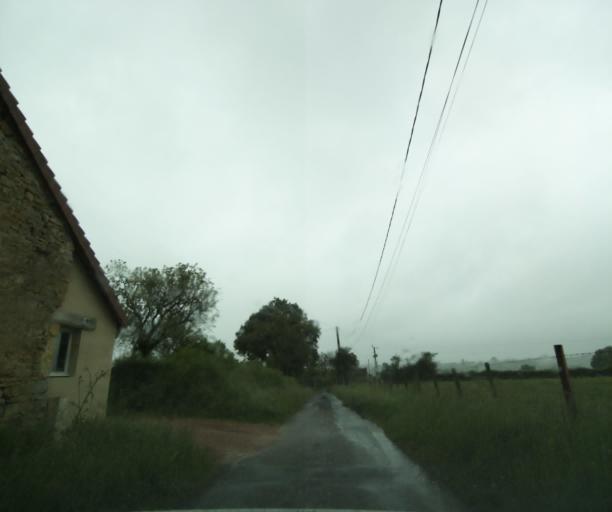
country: FR
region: Bourgogne
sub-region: Departement de Saone-et-Loire
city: Ciry-le-Noble
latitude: 46.5377
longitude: 4.3590
